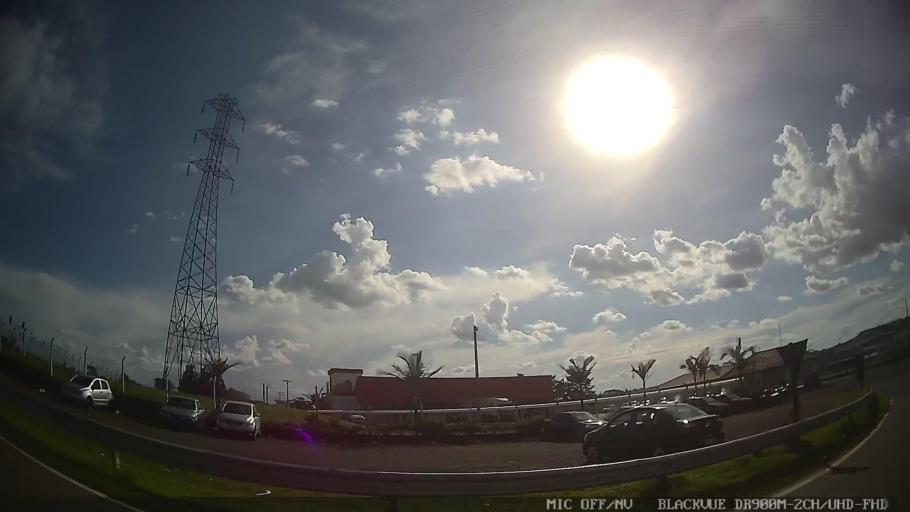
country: BR
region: Sao Paulo
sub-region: Laranjal Paulista
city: Laranjal Paulista
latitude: -23.0685
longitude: -47.8159
